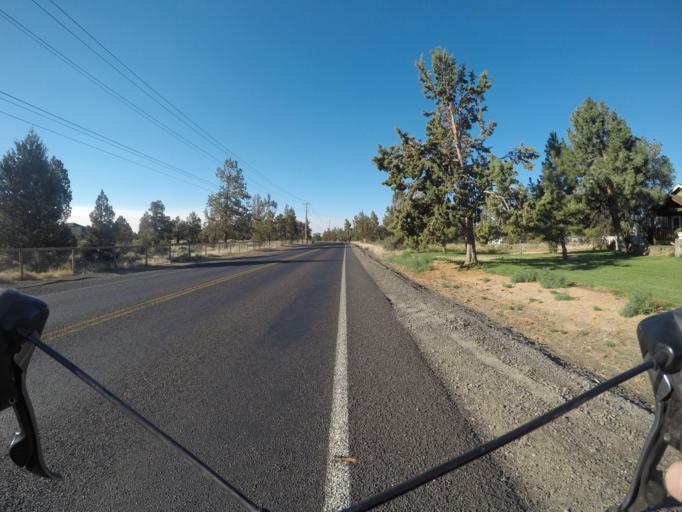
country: US
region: Oregon
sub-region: Deschutes County
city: Redmond
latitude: 44.2256
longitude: -121.2297
